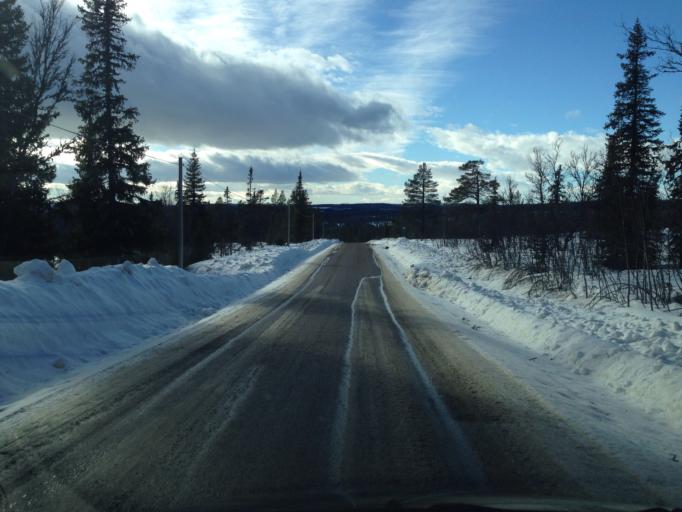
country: SE
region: Jaemtland
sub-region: Harjedalens Kommun
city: Sveg
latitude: 62.1322
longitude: 13.2733
